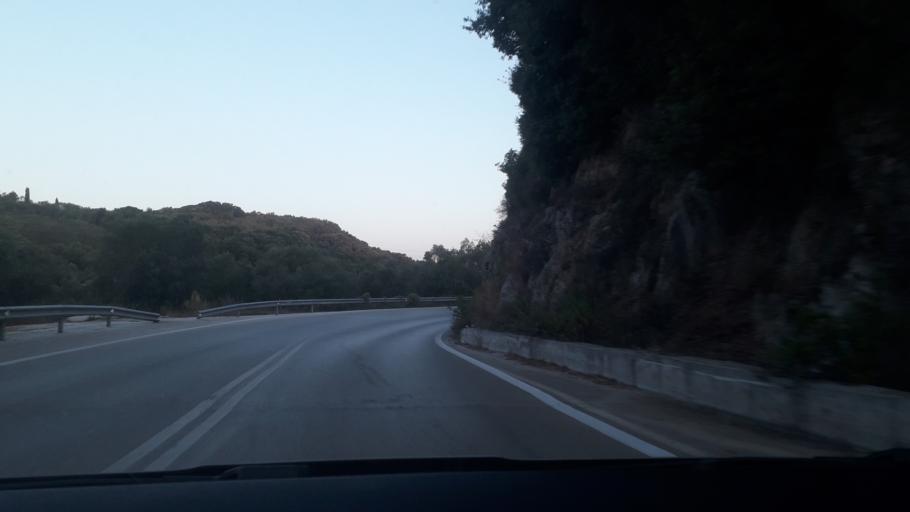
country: GR
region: Ionian Islands
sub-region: Nomos Kerkyras
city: Agios Matthaios
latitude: 39.4617
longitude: 19.9131
